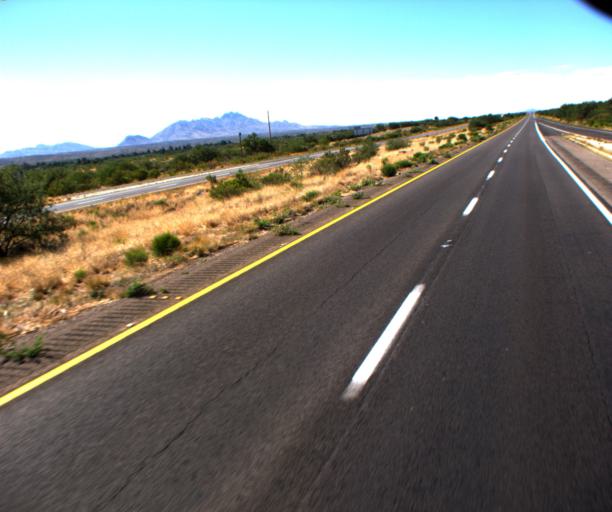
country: US
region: Arizona
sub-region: Santa Cruz County
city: Tubac
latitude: 31.6501
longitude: -111.0592
